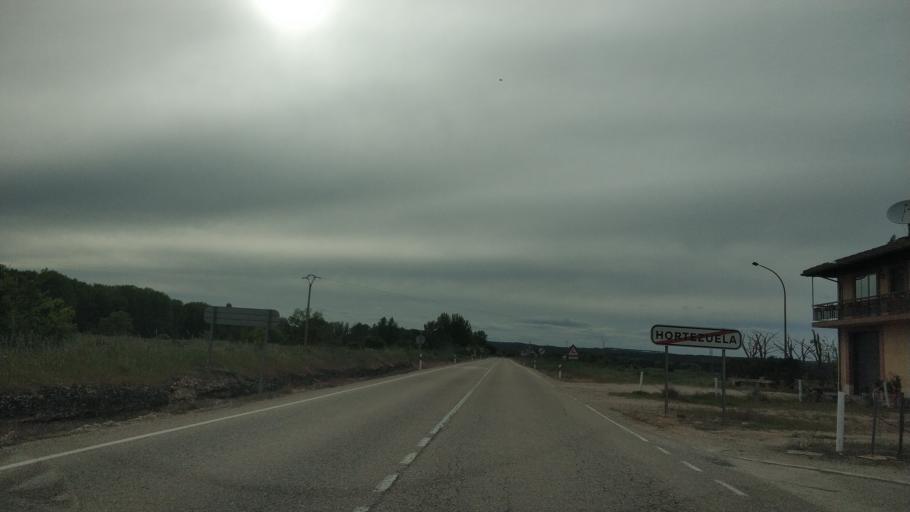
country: ES
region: Castille and Leon
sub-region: Provincia de Soria
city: Berlanga de Duero
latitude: 41.4958
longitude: -2.8710
